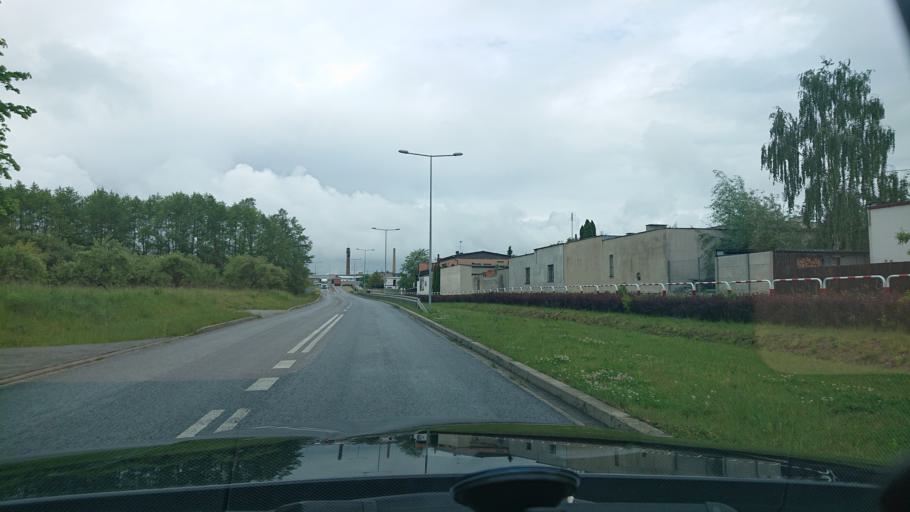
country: PL
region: Greater Poland Voivodeship
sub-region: Powiat gnieznienski
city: Gniezno
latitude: 52.5188
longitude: 17.6141
